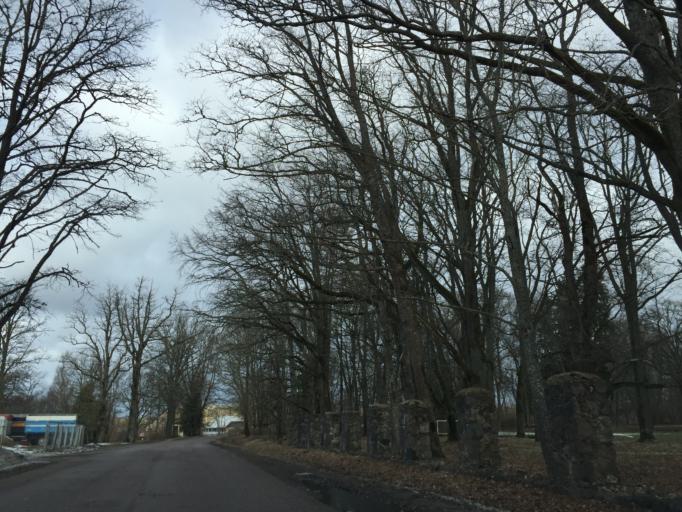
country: LV
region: Aloja
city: Aloja
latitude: 57.7721
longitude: 24.8127
